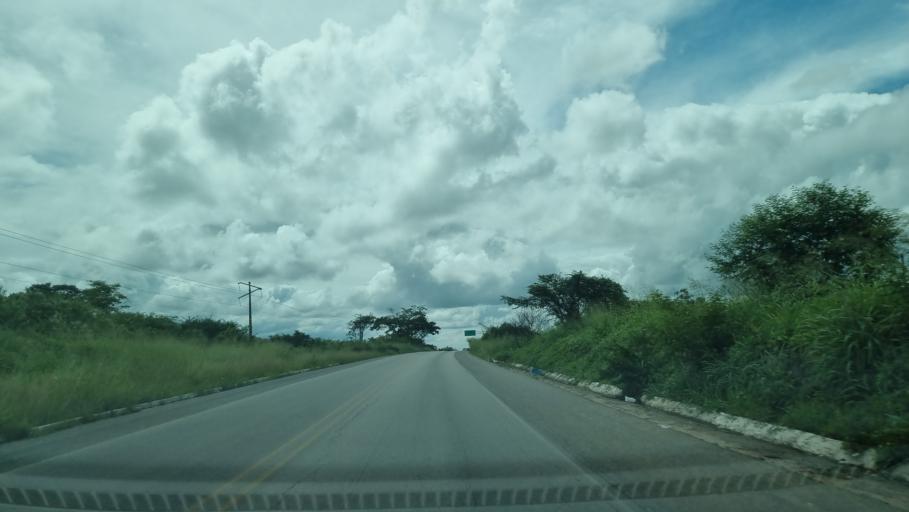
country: BR
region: Pernambuco
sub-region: Caruaru
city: Caruaru
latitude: -8.3448
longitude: -35.9833
